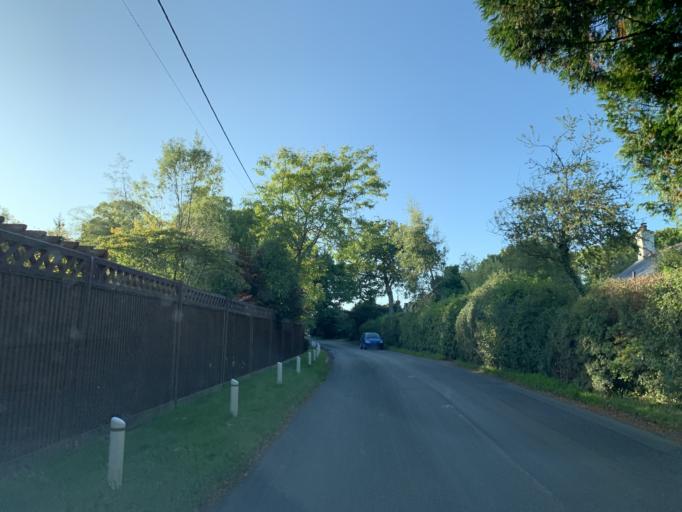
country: GB
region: England
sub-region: Wiltshire
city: Whiteparish
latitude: 50.9733
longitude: -1.6380
